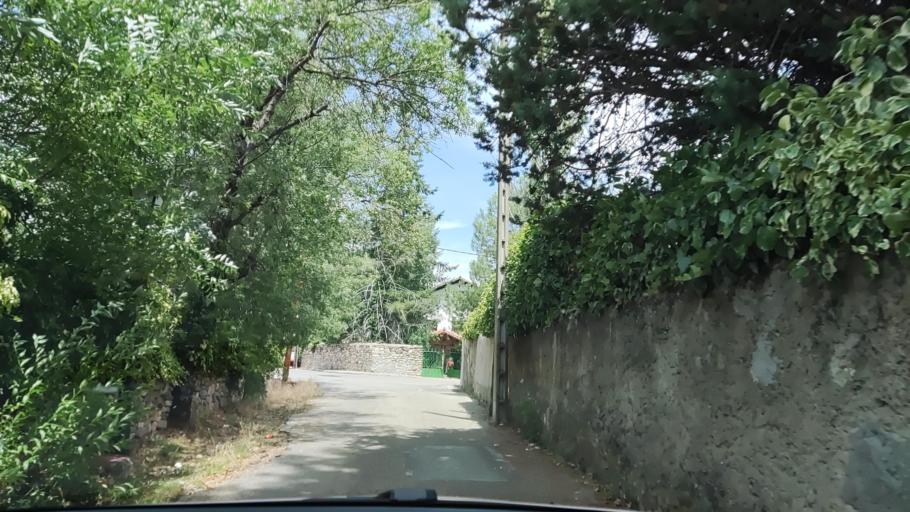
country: ES
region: Madrid
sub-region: Provincia de Madrid
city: Rascafria
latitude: 40.9029
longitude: -3.8816
